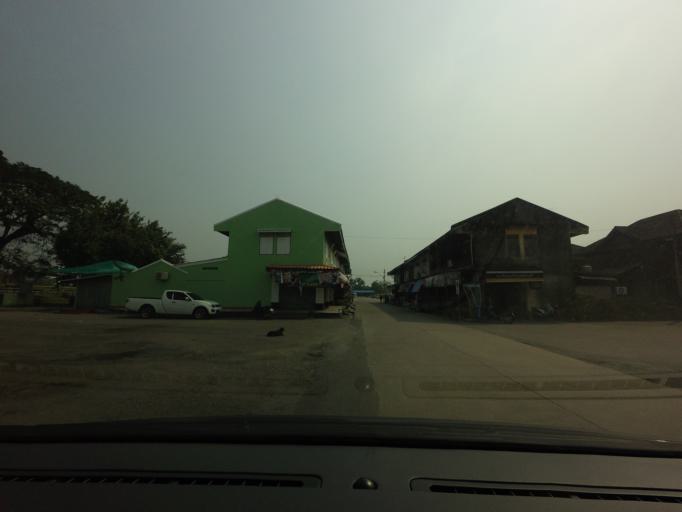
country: TH
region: Prachuap Khiri Khan
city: Kui Buri
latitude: 12.0694
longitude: 99.8716
